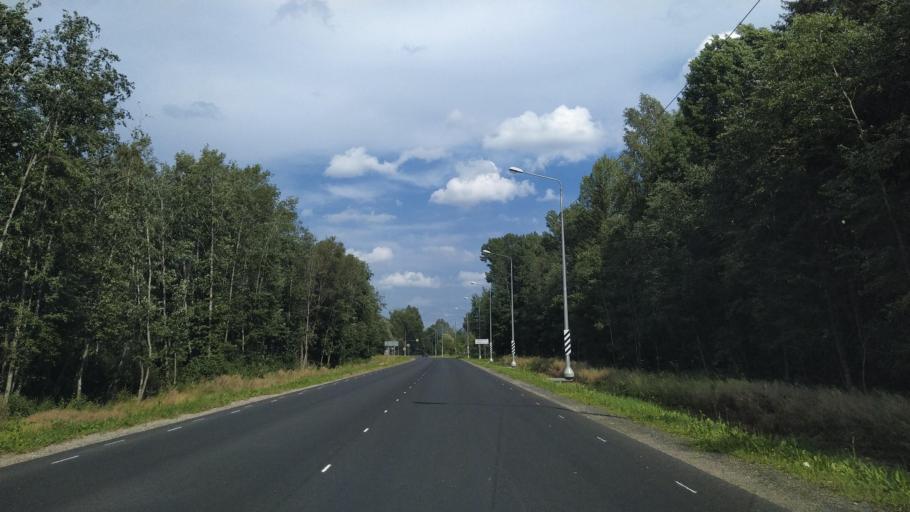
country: RU
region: Pskov
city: Vybor
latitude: 57.7301
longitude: 28.9710
